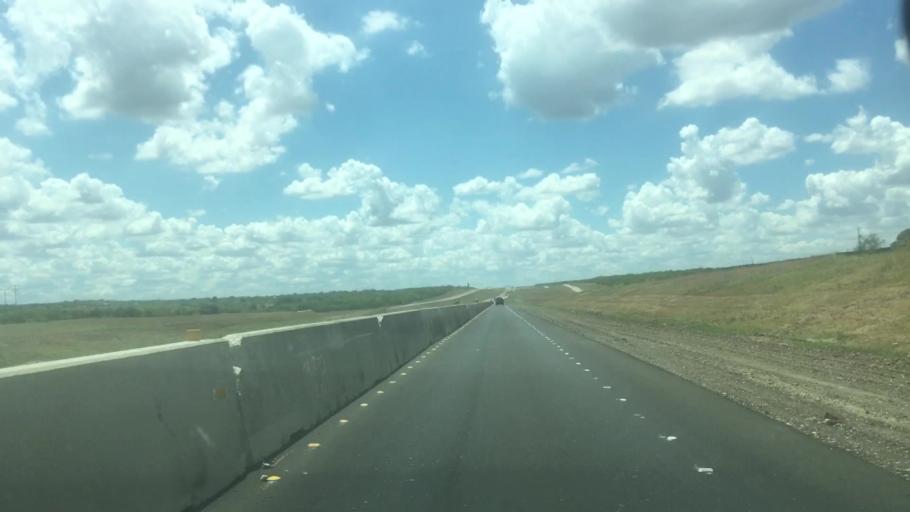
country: US
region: Texas
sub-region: Caldwell County
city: Lockhart
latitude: 29.8314
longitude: -97.7400
